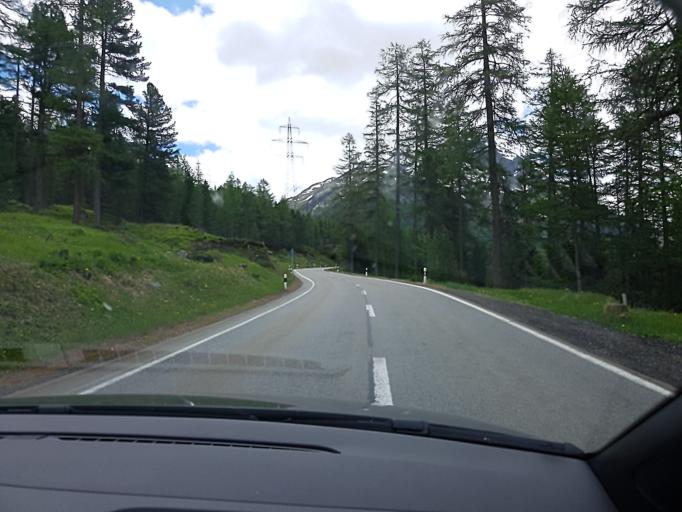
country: CH
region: Grisons
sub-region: Maloja District
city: Pontresina
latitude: 46.4611
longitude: 9.9391
